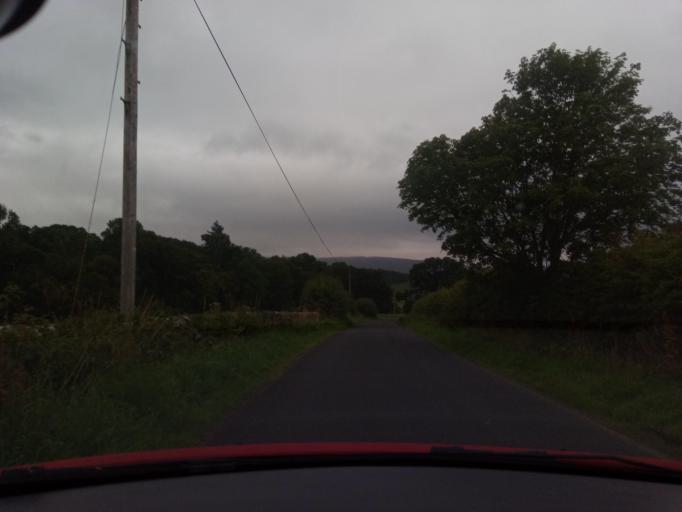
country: GB
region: England
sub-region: Northumberland
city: Otterburn
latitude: 55.3049
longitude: -2.0561
